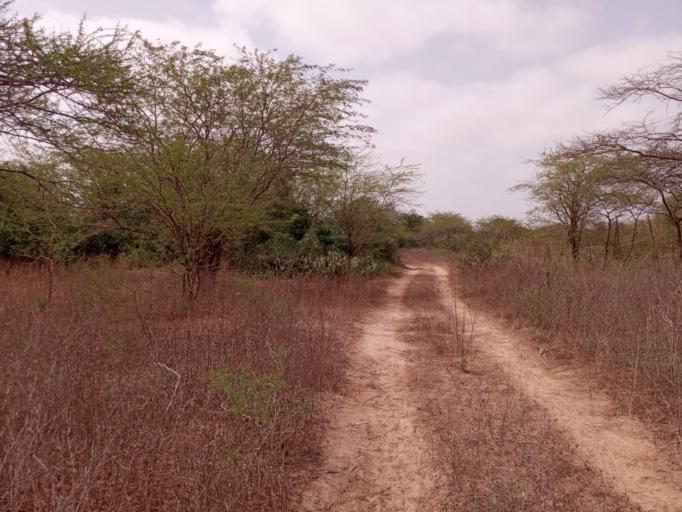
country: SN
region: Saint-Louis
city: Saint-Louis
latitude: 15.9190
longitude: -16.4530
